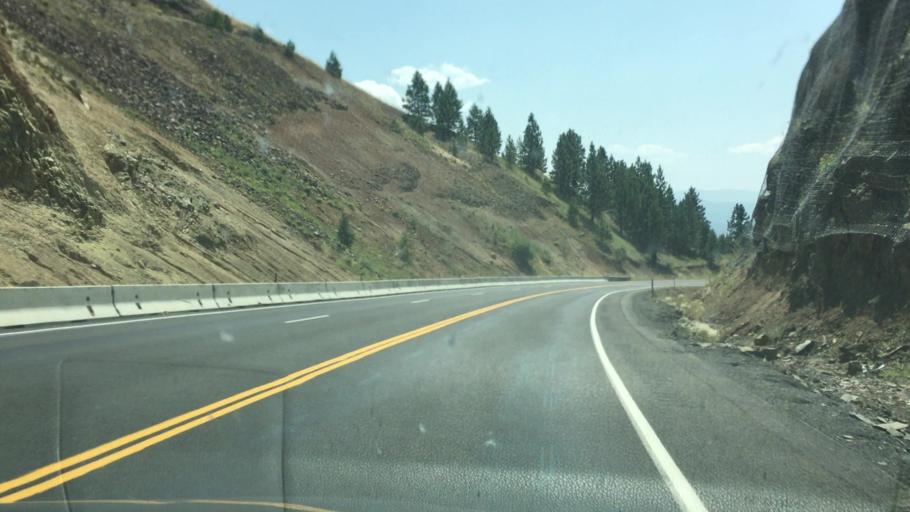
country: US
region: Idaho
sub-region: Idaho County
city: Grangeville
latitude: 45.8433
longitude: -116.2367
